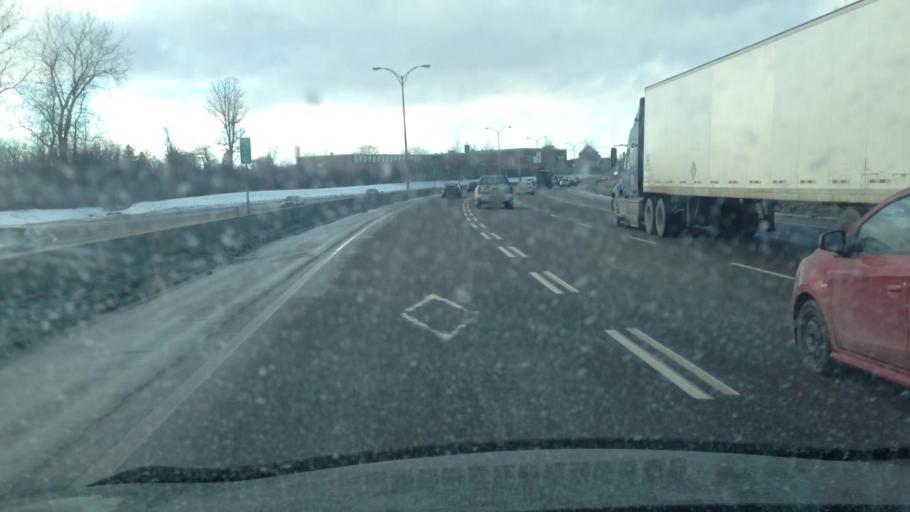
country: CA
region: Quebec
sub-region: Laval
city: Laval
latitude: 45.5322
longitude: -73.6898
